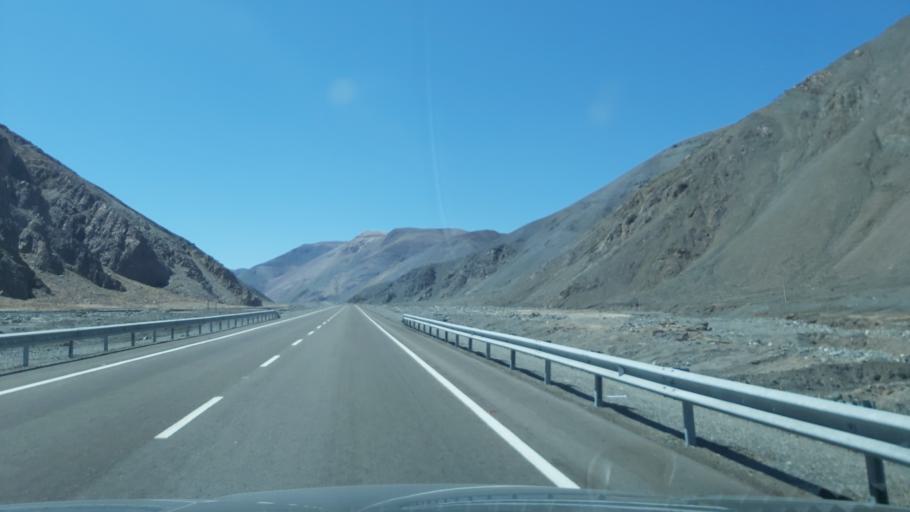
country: CL
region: Atacama
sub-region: Provincia de Chanaral
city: Diego de Almagro
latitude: -26.3502
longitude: -69.7384
